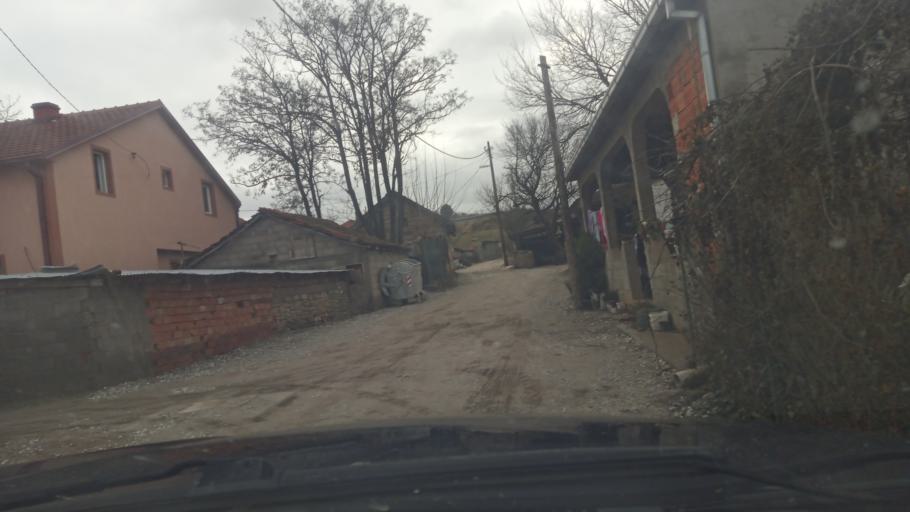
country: MK
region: Gradsko
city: Gradsko
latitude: 41.5812
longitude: 21.9295
